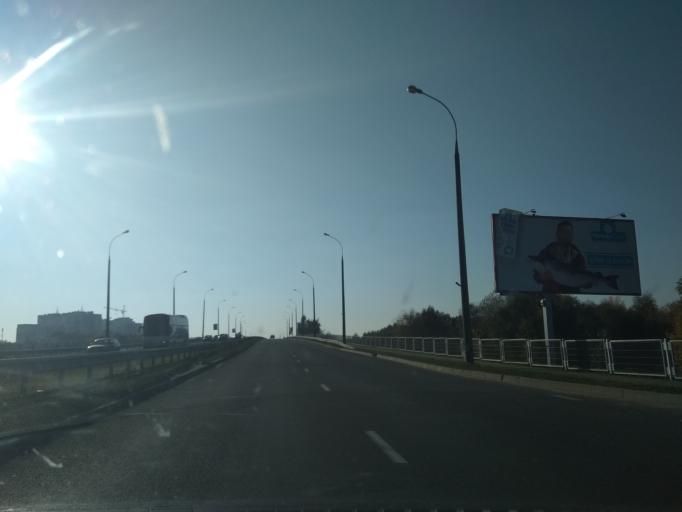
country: BY
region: Brest
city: Brest
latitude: 52.0799
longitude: 23.7348
